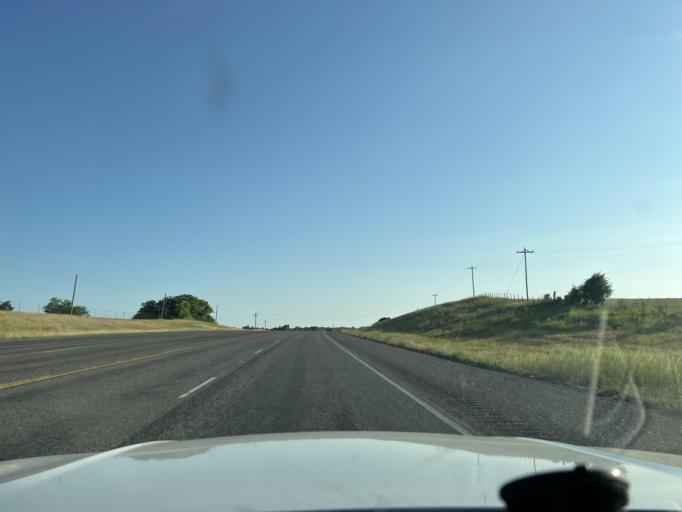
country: US
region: Texas
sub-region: Washington County
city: Brenham
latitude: 30.1916
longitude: -96.3696
